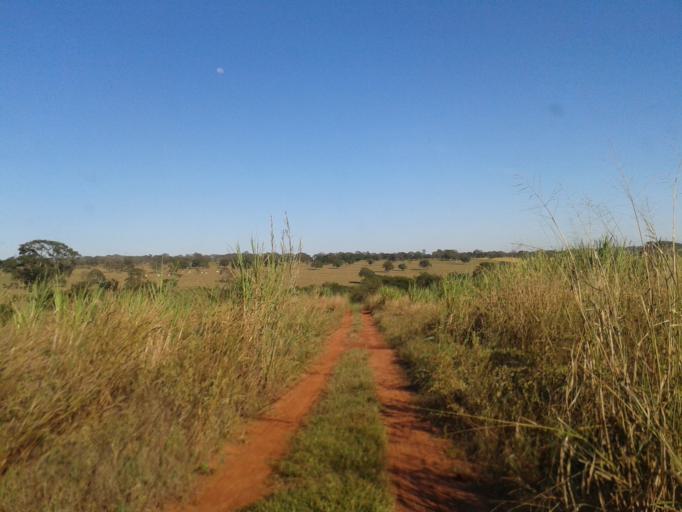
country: BR
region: Minas Gerais
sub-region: Santa Vitoria
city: Santa Vitoria
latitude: -19.0200
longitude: -50.3779
